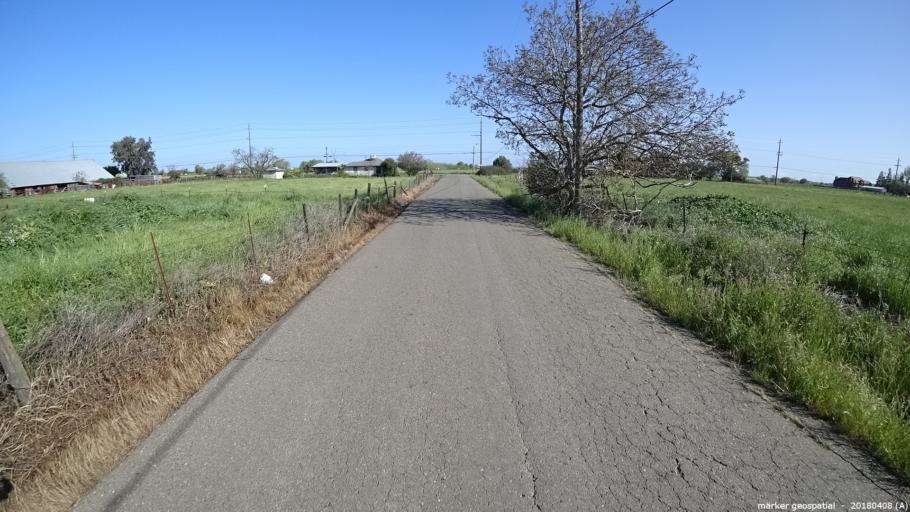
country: US
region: California
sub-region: Sacramento County
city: Elk Grove
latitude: 38.3714
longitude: -121.4038
